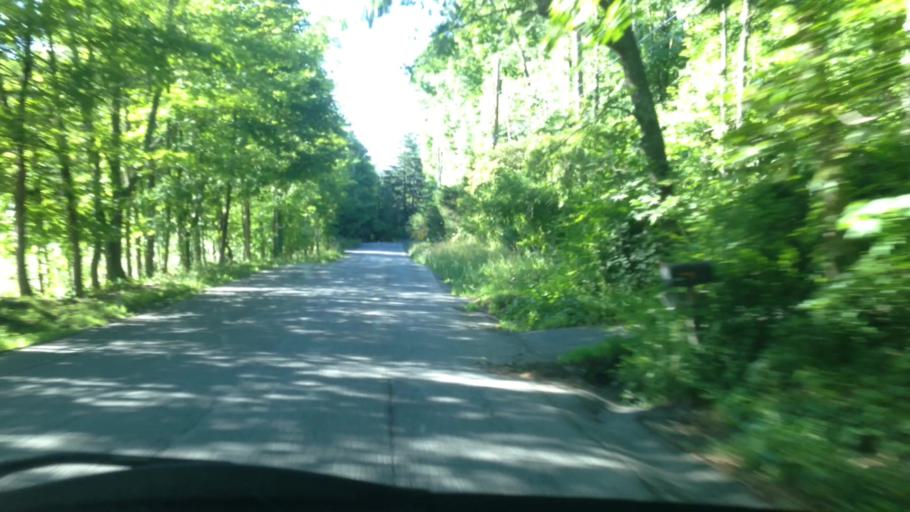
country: US
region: New York
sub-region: Ulster County
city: Tillson
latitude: 41.8170
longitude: -74.0451
